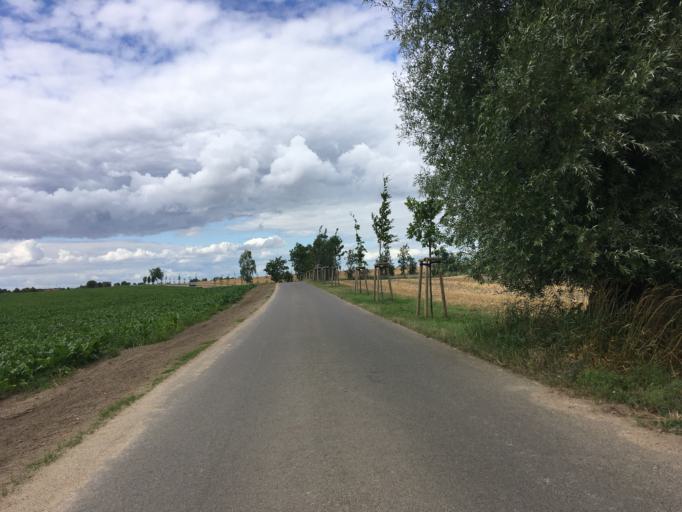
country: DE
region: Brandenburg
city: Gramzow
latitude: 53.2642
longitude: 14.0168
